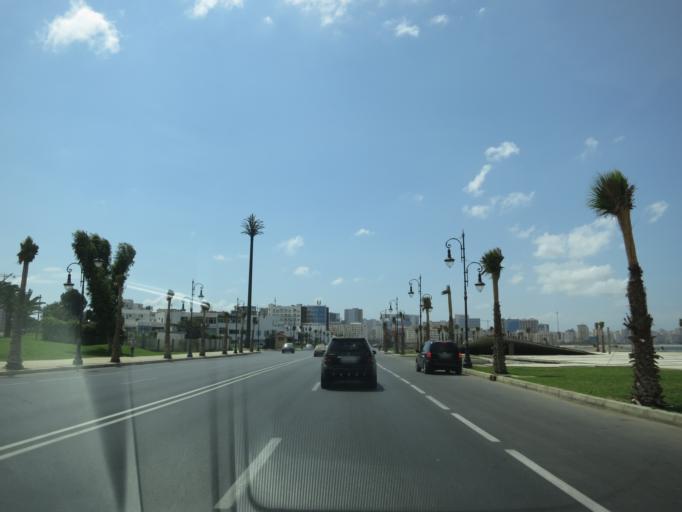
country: MA
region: Tanger-Tetouan
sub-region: Tanger-Assilah
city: Tangier
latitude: 35.7785
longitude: -5.7743
